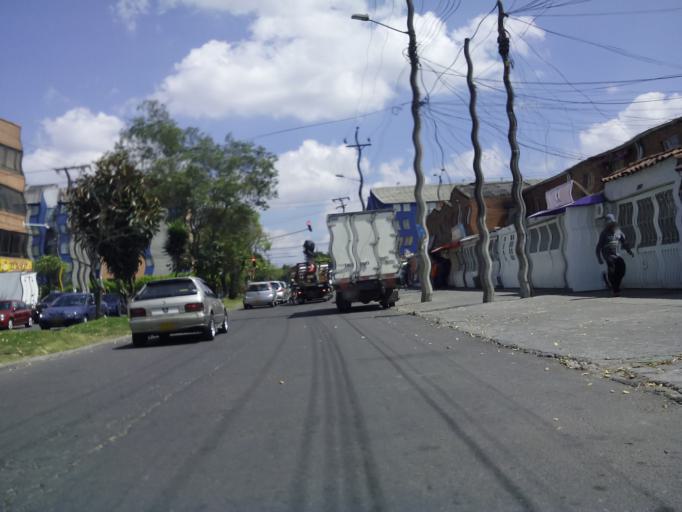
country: CO
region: Bogota D.C.
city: Bogota
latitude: 4.6796
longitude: -74.1332
